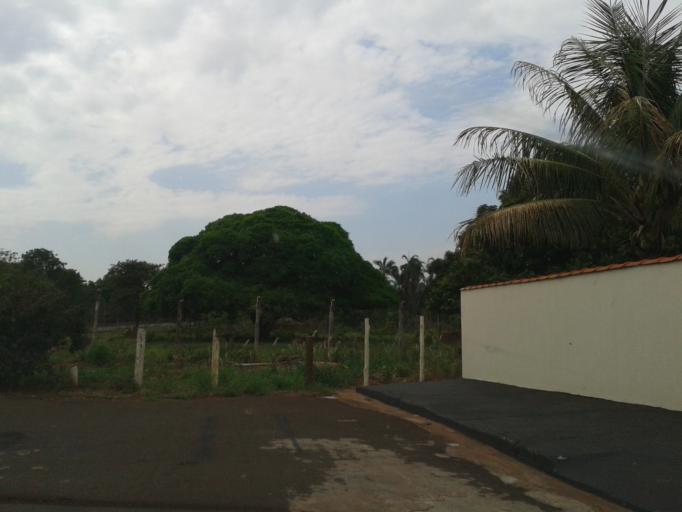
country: BR
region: Minas Gerais
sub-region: Ituiutaba
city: Ituiutaba
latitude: -18.9778
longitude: -49.4428
